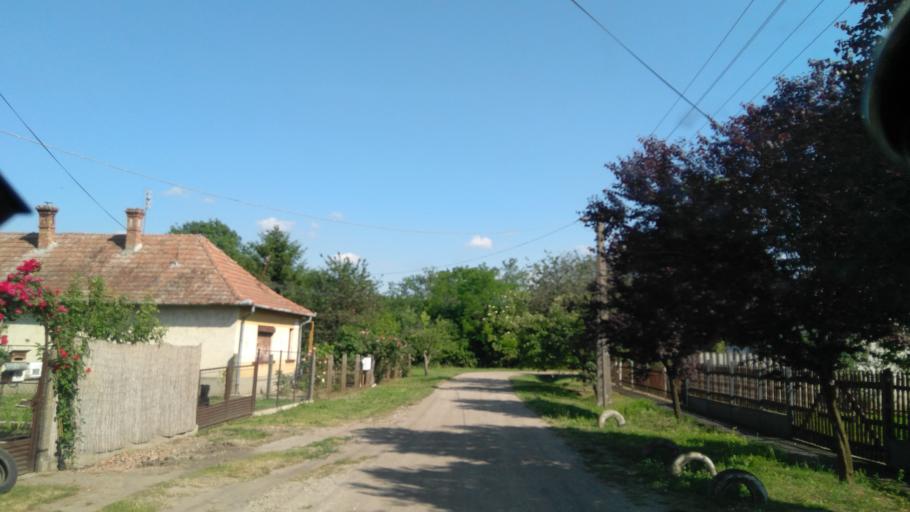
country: HU
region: Bekes
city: Doboz
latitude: 46.7003
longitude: 21.1912
